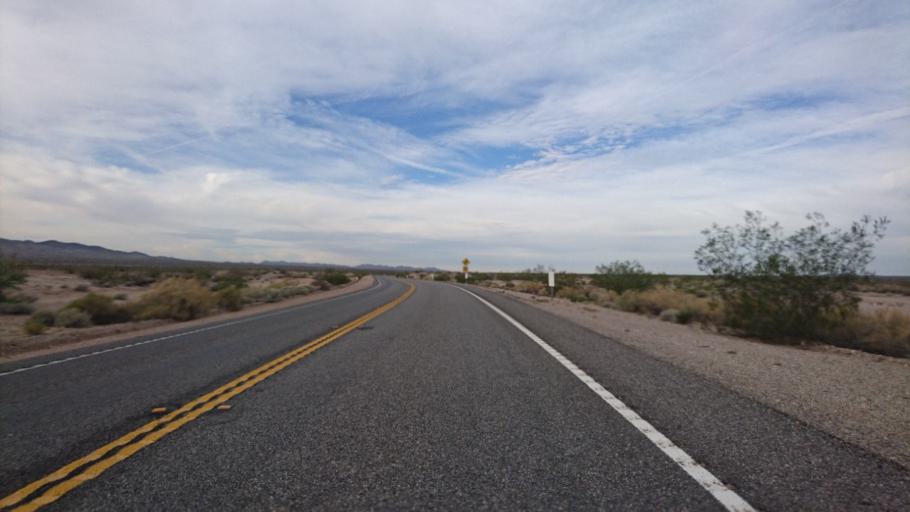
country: US
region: Arizona
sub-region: Mohave County
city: Willow Valley
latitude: 34.9409
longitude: -114.8175
